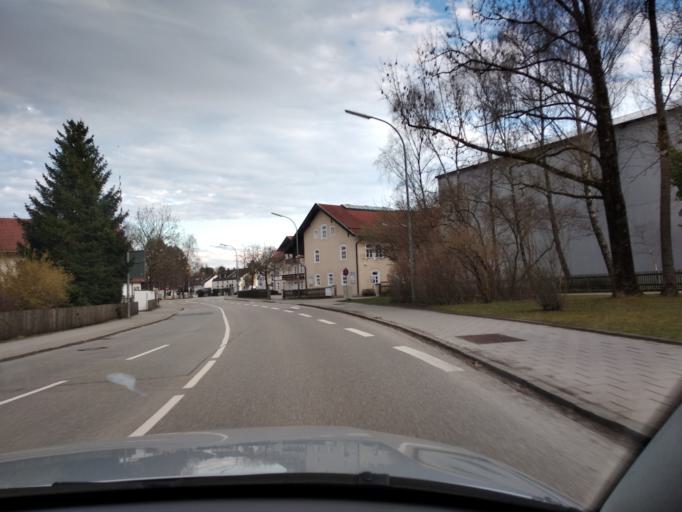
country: DE
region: Bavaria
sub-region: Upper Bavaria
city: Unterhaching
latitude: 48.0610
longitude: 11.6169
